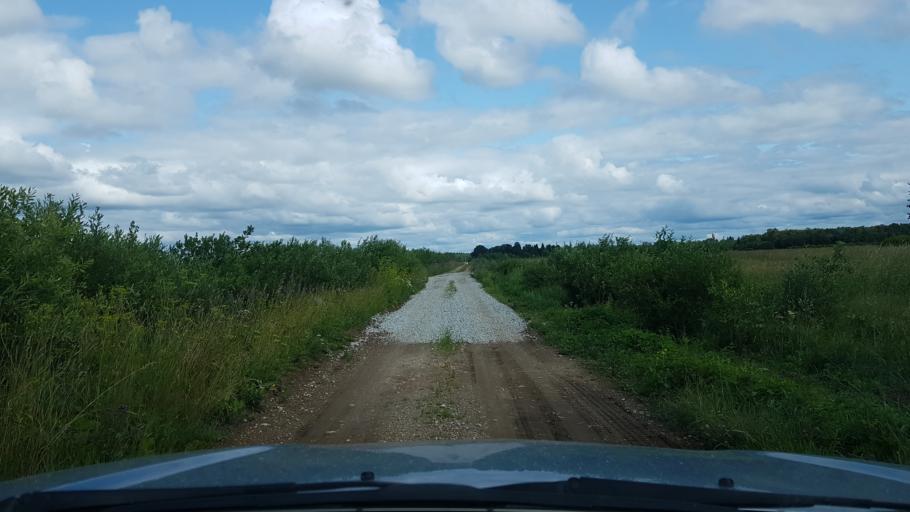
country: EE
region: Ida-Virumaa
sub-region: Narva-Joesuu linn
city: Narva-Joesuu
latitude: 59.3701
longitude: 27.9329
